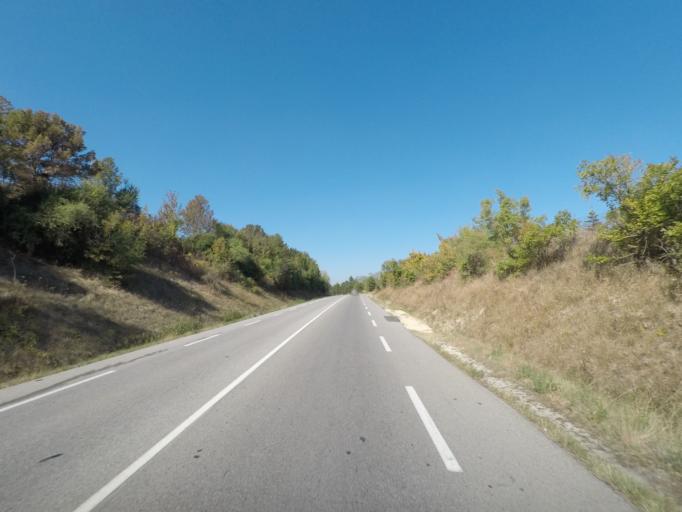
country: FR
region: Rhone-Alpes
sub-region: Departement de la Drome
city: Crest
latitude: 44.7211
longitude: 5.0221
